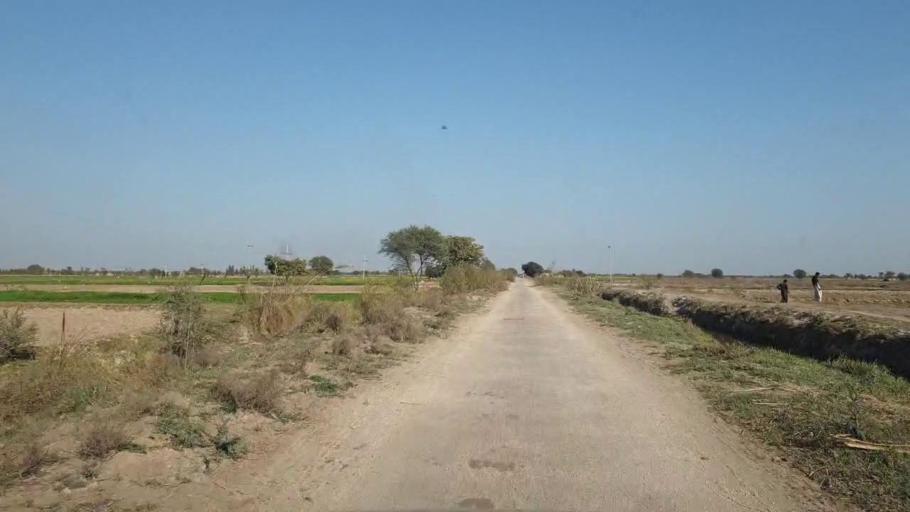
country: PK
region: Sindh
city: Tando Allahyar
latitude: 25.3902
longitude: 68.6944
